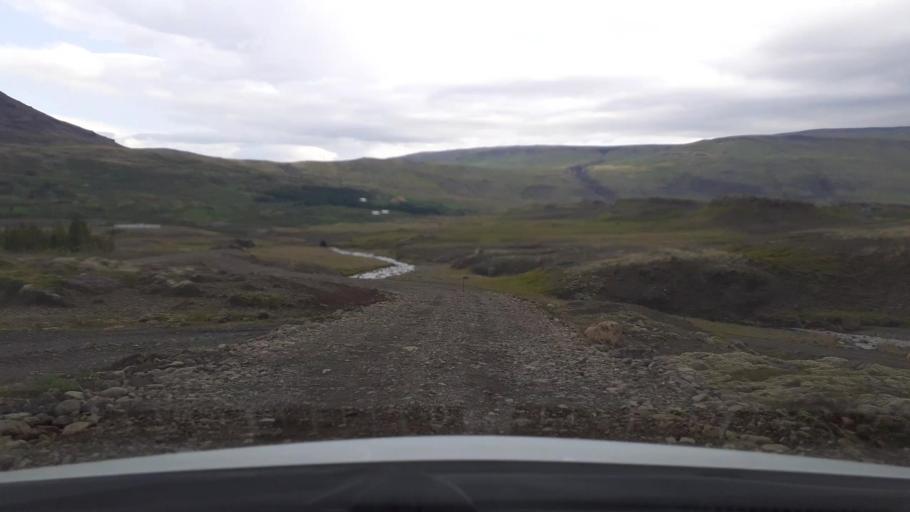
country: IS
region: Capital Region
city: Mosfellsbaer
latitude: 64.2879
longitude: -21.4617
